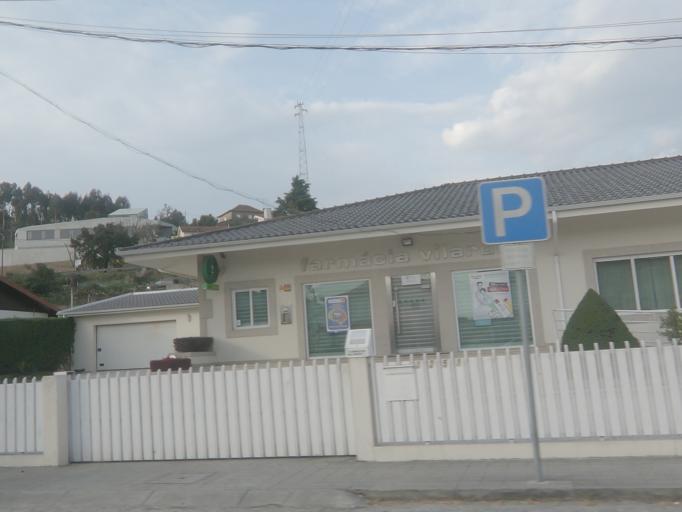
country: PT
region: Porto
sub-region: Valongo
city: Campo
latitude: 41.1835
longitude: -8.4699
